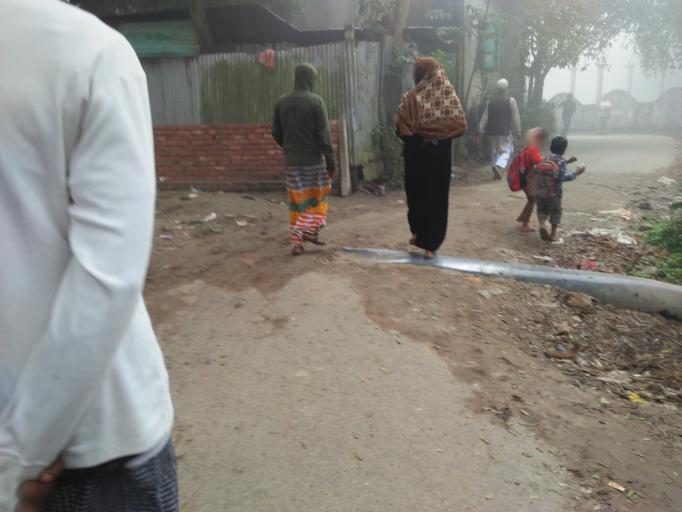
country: BD
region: Dhaka
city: Azimpur
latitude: 23.6878
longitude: 90.3029
